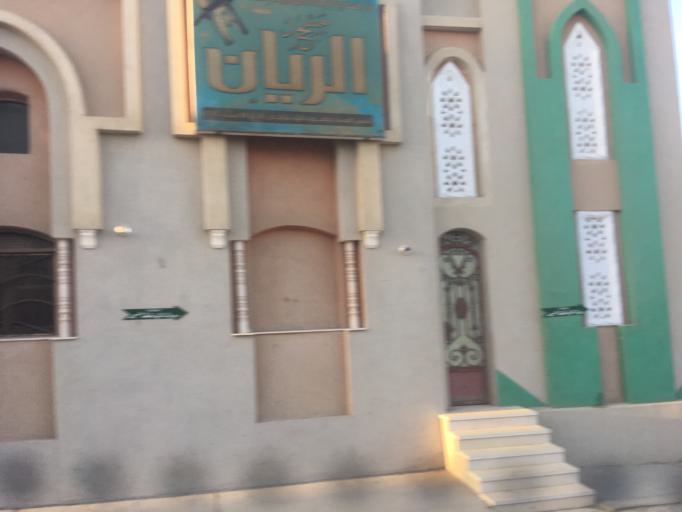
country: EG
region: Red Sea
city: Al Qusayr
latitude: 26.1071
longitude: 34.2850
